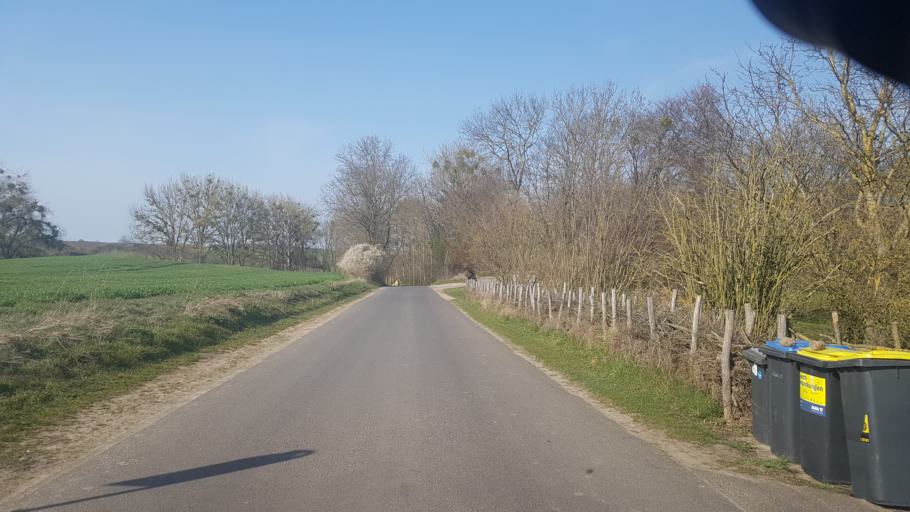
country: DE
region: Brandenburg
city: Gerswalde
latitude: 53.1972
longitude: 13.7817
